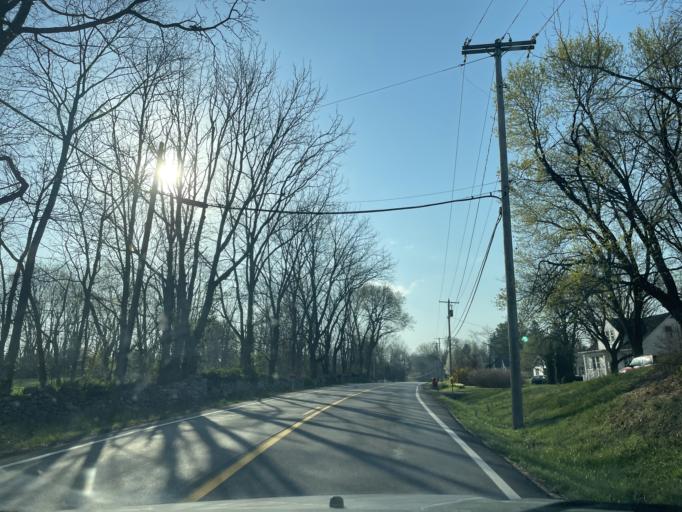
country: US
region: Maryland
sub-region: Washington County
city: Saint James
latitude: 39.5496
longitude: -77.7289
